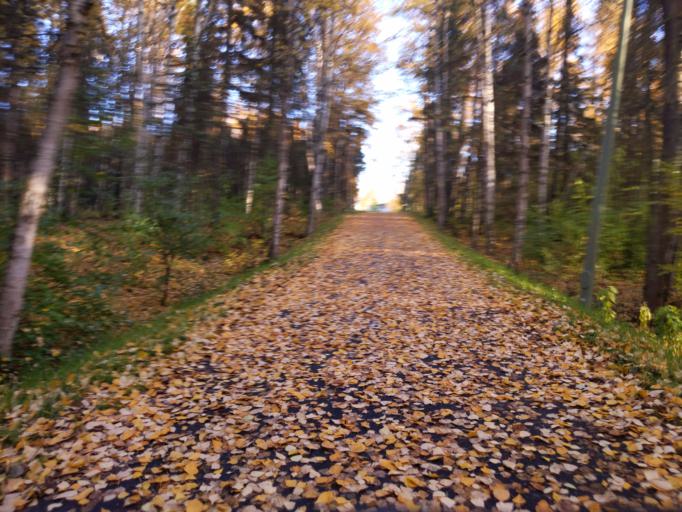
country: US
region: Alaska
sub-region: Anchorage Municipality
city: Anchorage
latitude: 61.1560
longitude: -149.8739
